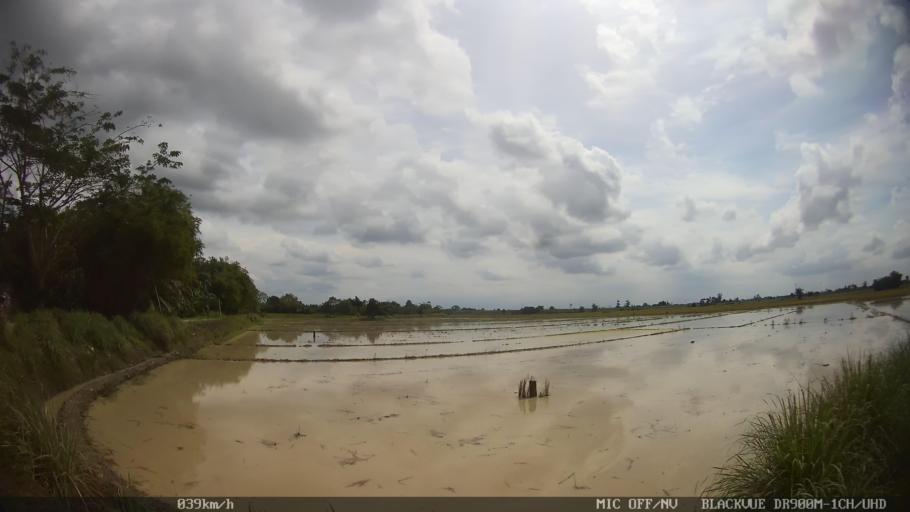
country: ID
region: North Sumatra
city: Percut
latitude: 3.5684
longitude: 98.8527
